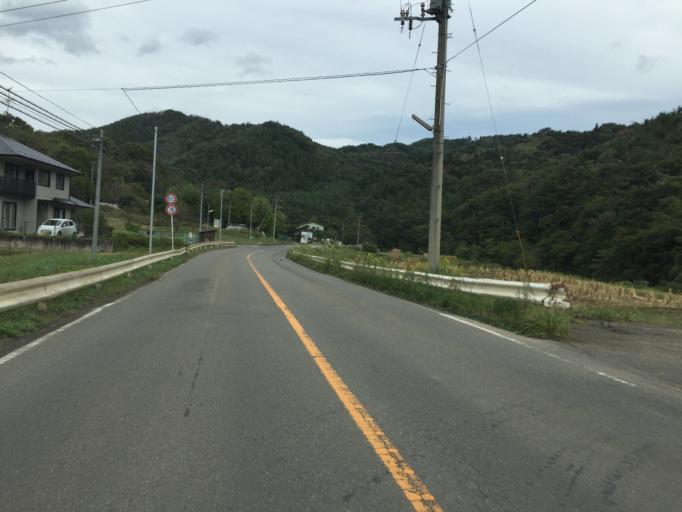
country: JP
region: Fukushima
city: Yanagawamachi-saiwaicho
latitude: 37.8723
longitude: 140.6428
